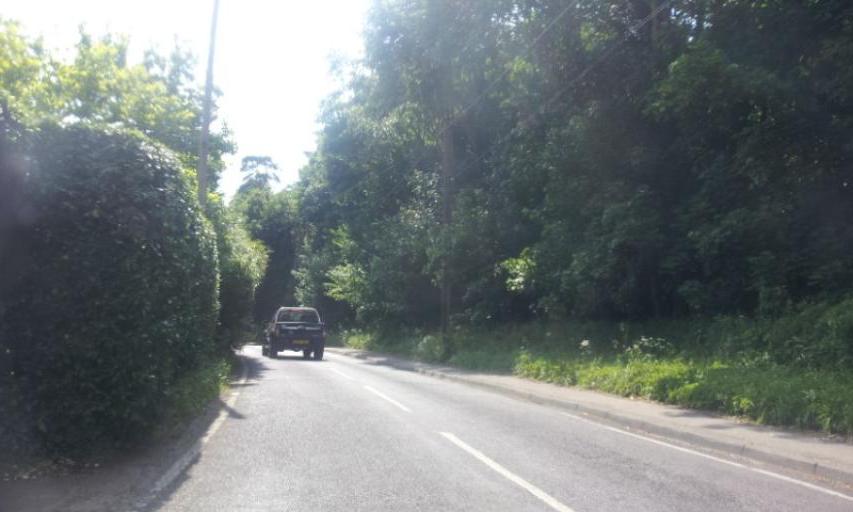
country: GB
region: England
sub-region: Kent
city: Teynham
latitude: 51.2835
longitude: 0.7952
